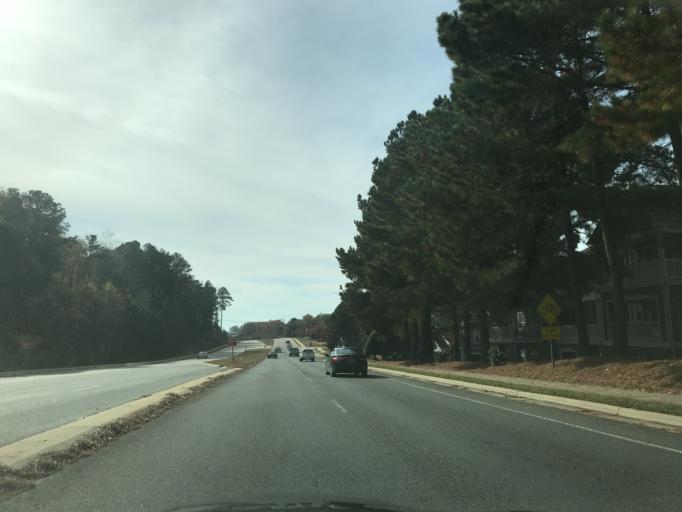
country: US
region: North Carolina
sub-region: Wake County
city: West Raleigh
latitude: 35.8235
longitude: -78.7074
